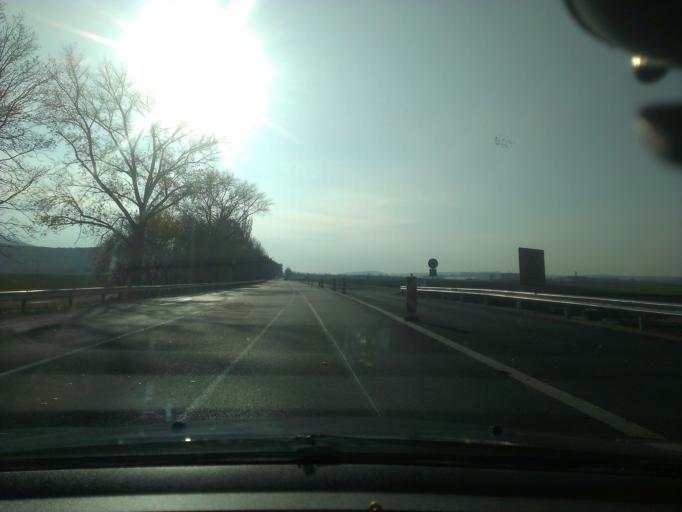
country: SK
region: Nitriansky
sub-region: Okres Nitra
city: Nitra
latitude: 48.3676
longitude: 18.0438
